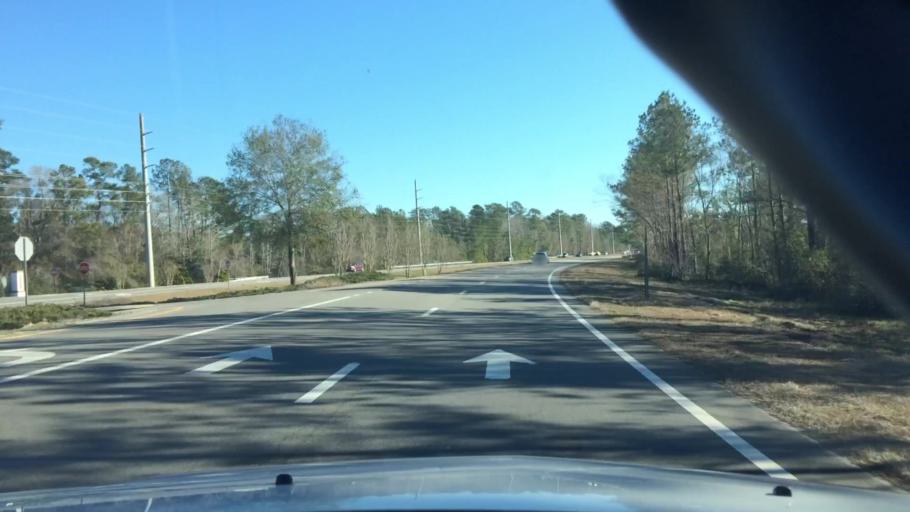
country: US
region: North Carolina
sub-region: Brunswick County
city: Carolina Shores
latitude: 33.9366
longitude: -78.5659
